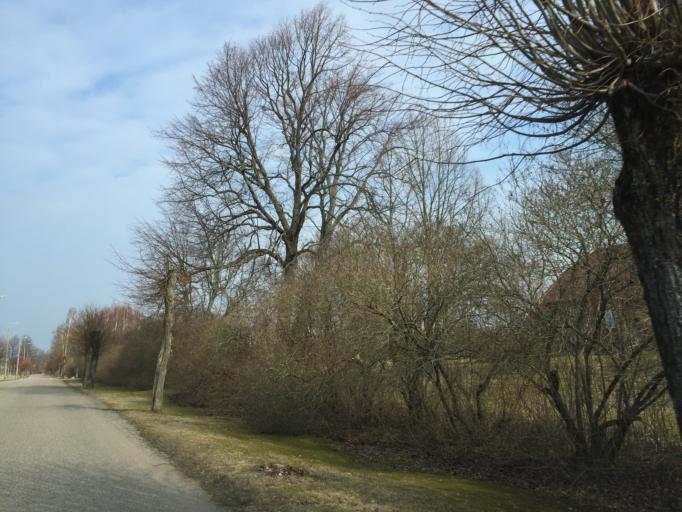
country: LV
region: Salacgrivas
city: Ainazi
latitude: 57.8667
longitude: 24.3596
